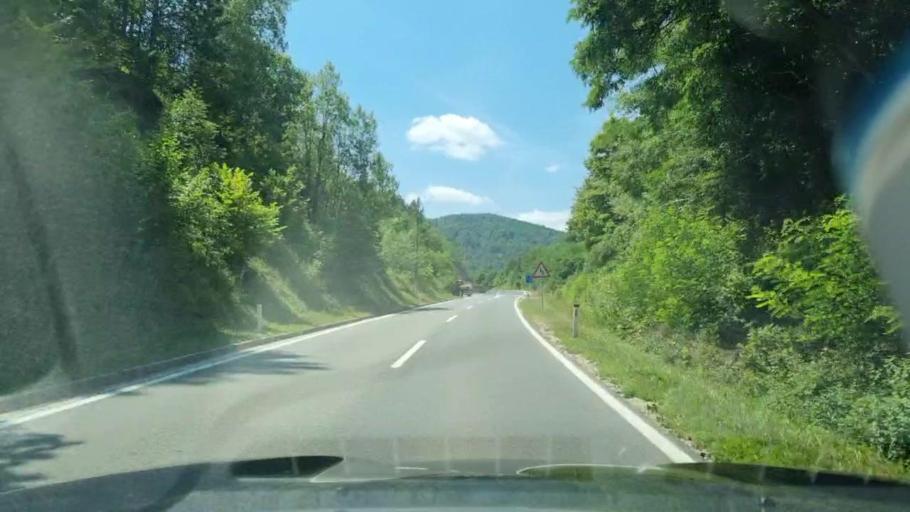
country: BA
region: Federation of Bosnia and Herzegovina
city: Velagici
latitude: 44.5512
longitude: 16.7023
